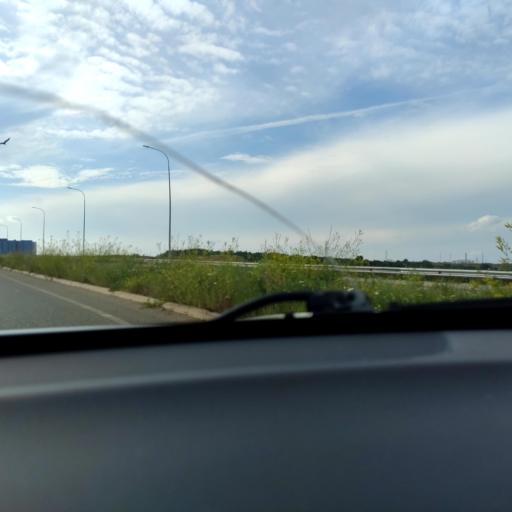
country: RU
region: Tatarstan
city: Sviyazhsk
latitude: 55.7466
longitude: 48.7660
